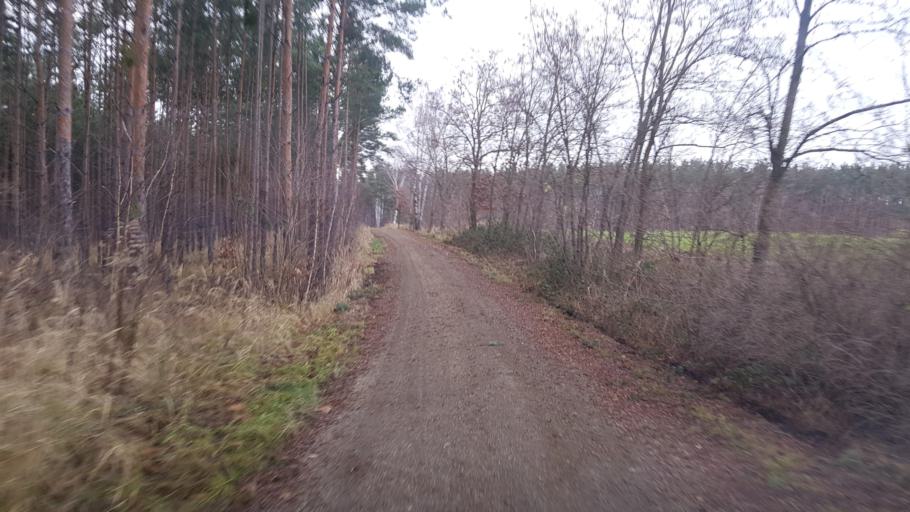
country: DE
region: Brandenburg
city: Lauchhammer
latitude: 51.5227
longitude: 13.6890
